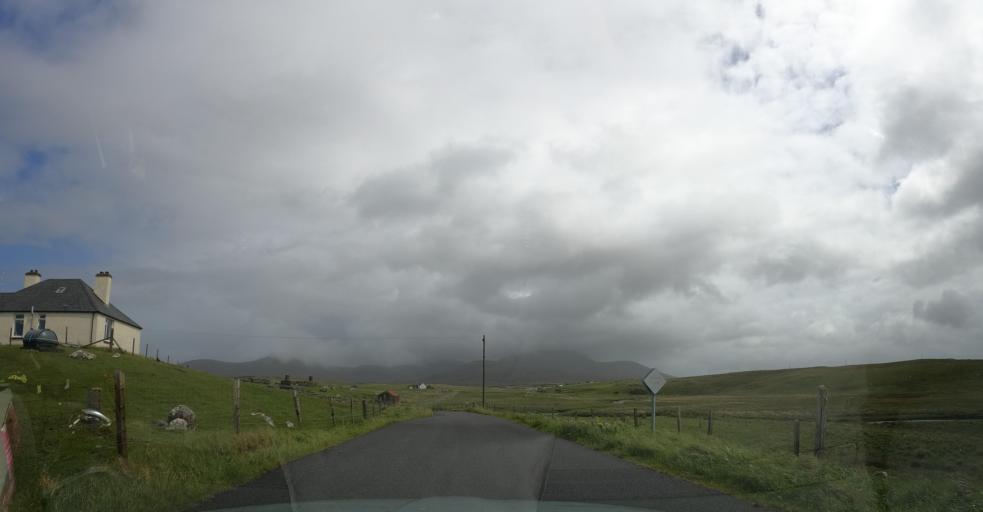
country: GB
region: Scotland
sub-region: Eilean Siar
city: Isle of South Uist
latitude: 57.2914
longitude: -7.3764
